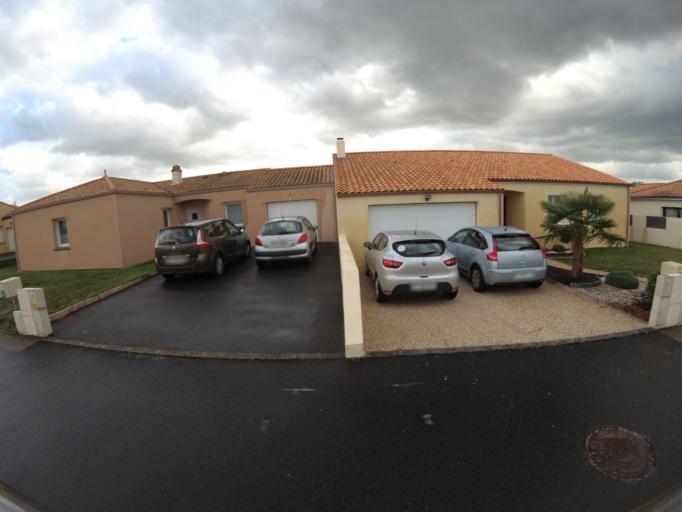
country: FR
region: Pays de la Loire
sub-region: Departement de la Loire-Atlantique
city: Saint-Hilaire-de-Clisson
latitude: 47.0650
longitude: -1.3120
